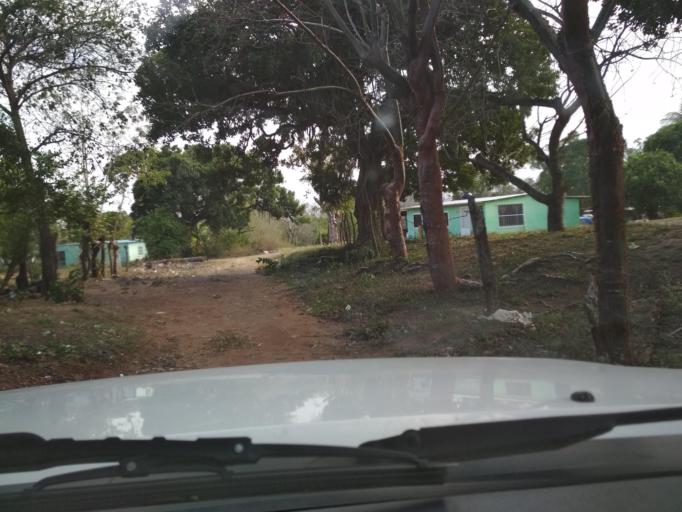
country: MX
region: Veracruz
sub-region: Veracruz
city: Delfino Victoria (Santa Fe)
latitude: 19.1507
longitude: -96.2998
